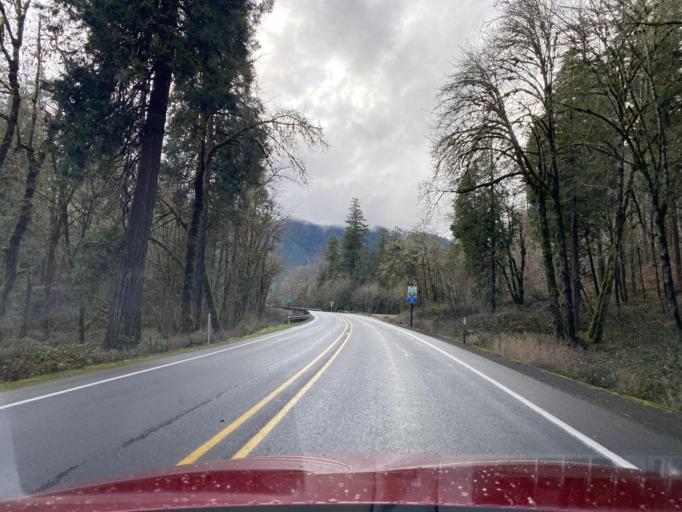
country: US
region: Oregon
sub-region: Lane County
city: Oakridge
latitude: 43.7481
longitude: -122.5068
